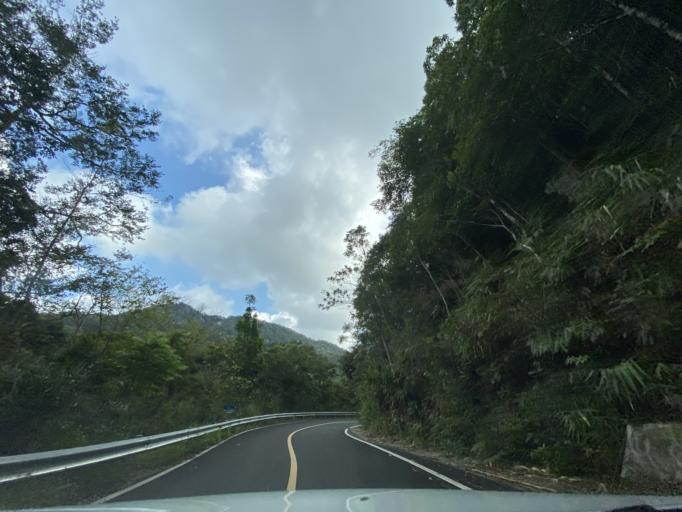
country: CN
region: Hainan
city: Diaoluoshan
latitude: 18.7040
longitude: 109.8823
